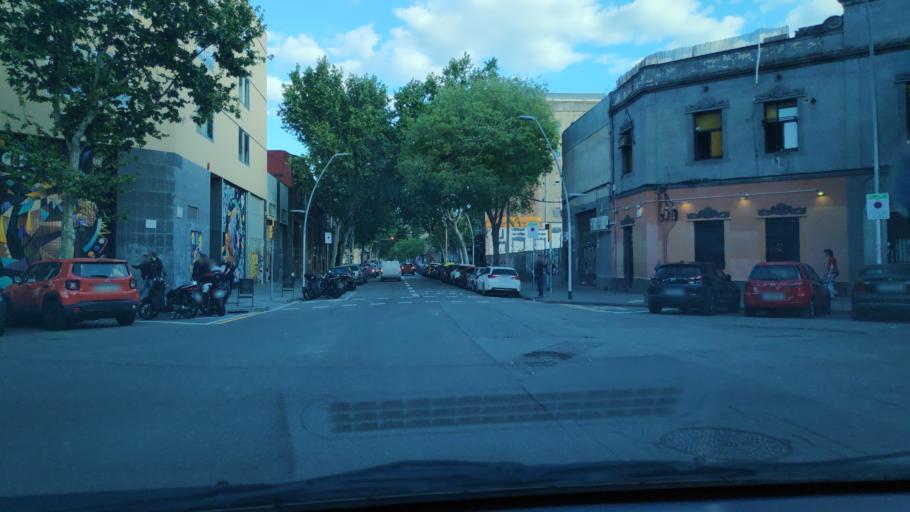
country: ES
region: Catalonia
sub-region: Provincia de Barcelona
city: Sant Marti
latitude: 41.3974
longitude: 2.1904
